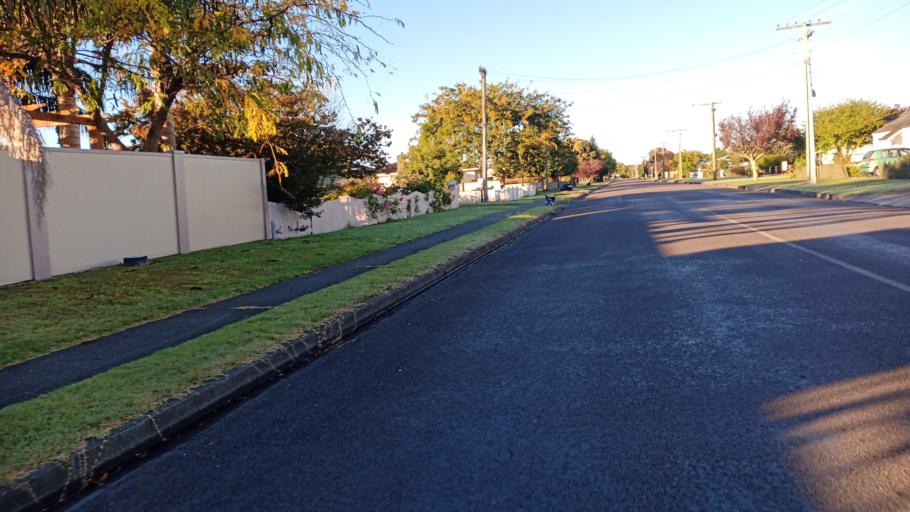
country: NZ
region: Gisborne
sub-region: Gisborne District
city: Gisborne
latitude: -38.6525
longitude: 177.9919
